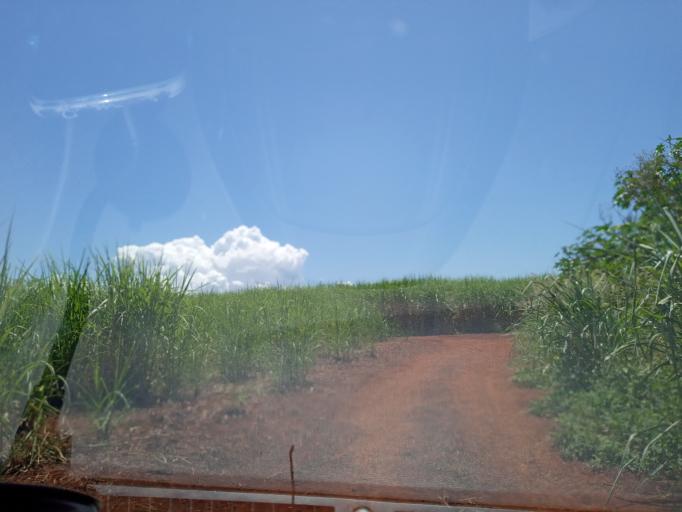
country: BR
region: Goias
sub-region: Itumbiara
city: Itumbiara
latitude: -18.4336
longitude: -49.1666
